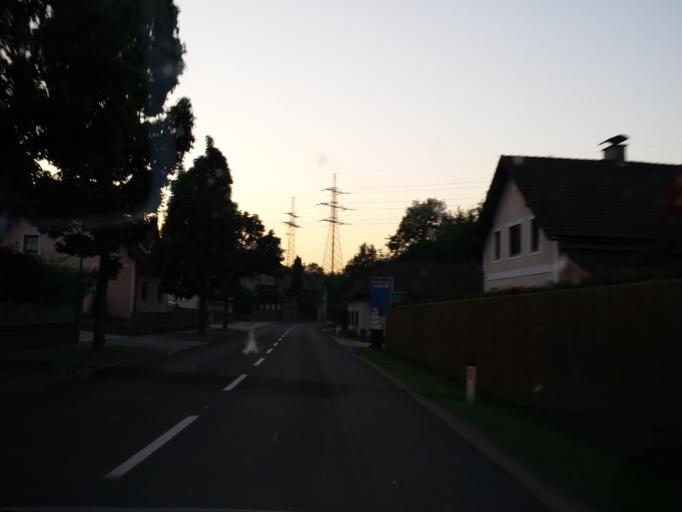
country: AT
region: Lower Austria
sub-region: Politischer Bezirk Lilienfeld
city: Hainfeld
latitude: 48.0290
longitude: 15.7747
